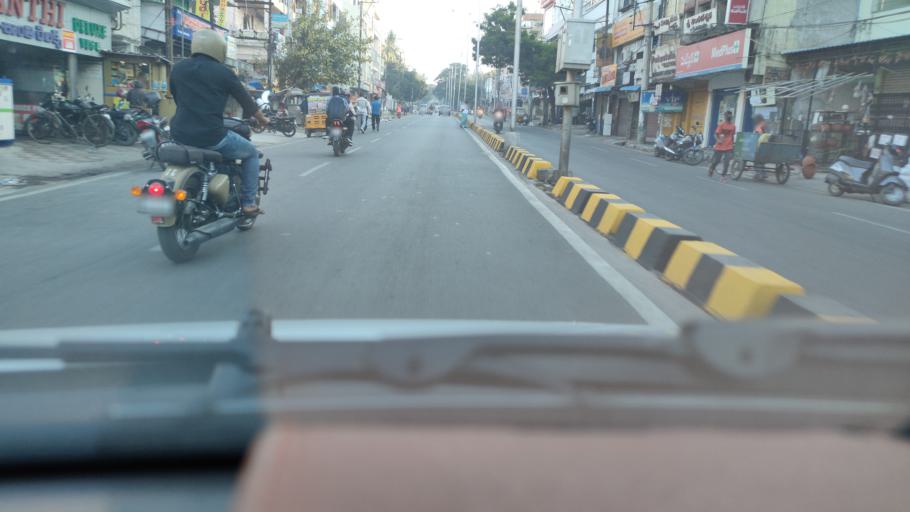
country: IN
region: Telangana
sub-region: Rangareddi
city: Gaddi Annaram
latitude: 17.3990
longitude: 78.5127
